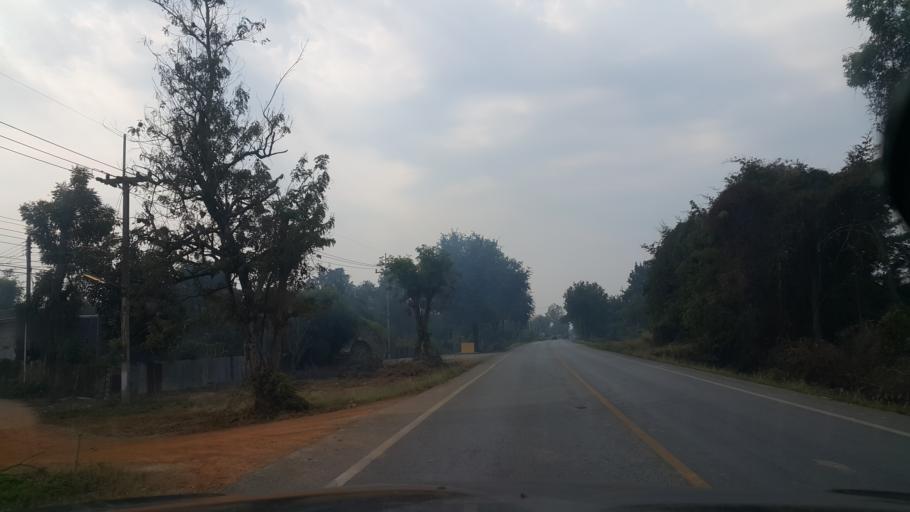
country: TH
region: Sukhothai
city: Si Samrong
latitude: 17.1068
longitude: 99.8888
